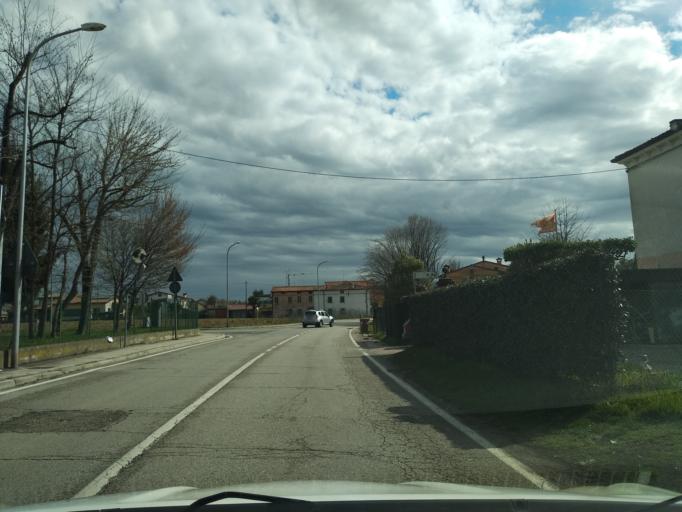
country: IT
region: Veneto
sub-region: Provincia di Vicenza
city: Monticello Conte Otto
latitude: 45.5969
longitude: 11.5774
